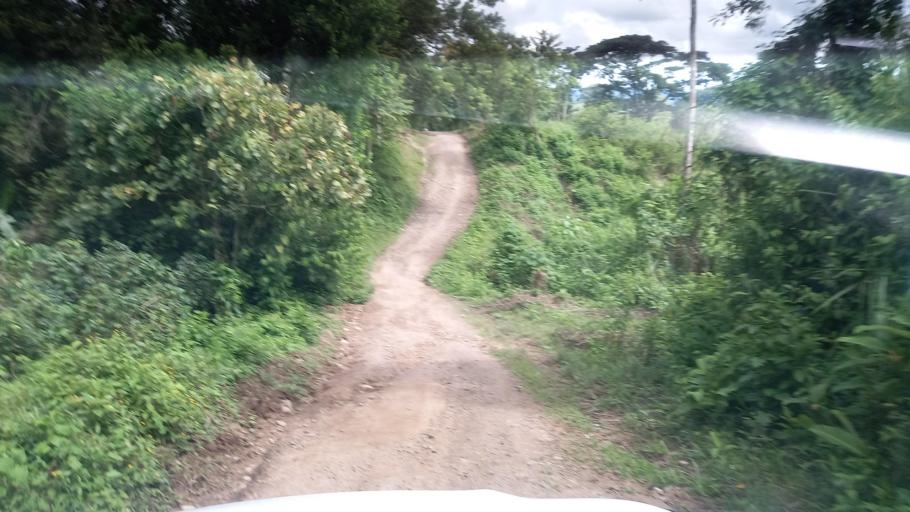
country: NI
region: Jinotega
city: San Jose de Bocay
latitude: 13.4128
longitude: -85.7029
